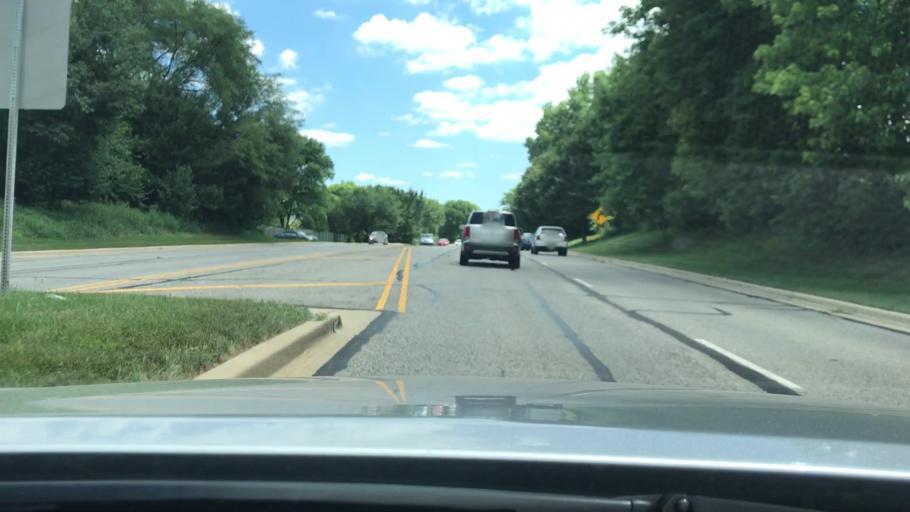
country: US
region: Illinois
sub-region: DuPage County
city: Naperville
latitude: 41.7854
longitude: -88.1131
